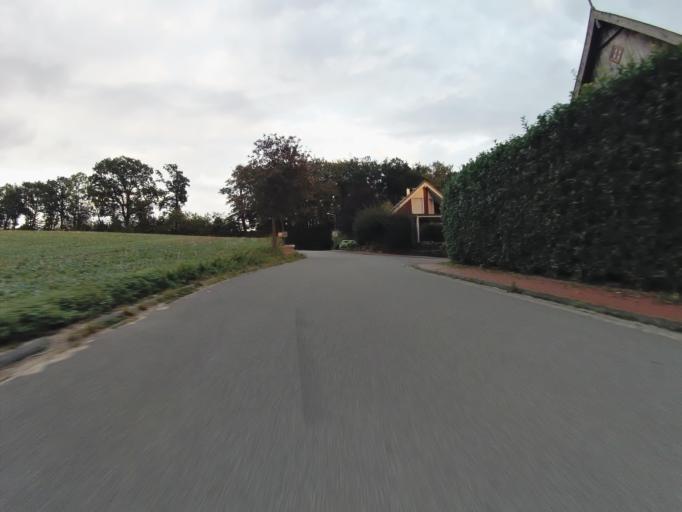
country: DE
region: North Rhine-Westphalia
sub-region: Regierungsbezirk Munster
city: Westerkappeln
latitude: 52.2712
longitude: 7.8621
